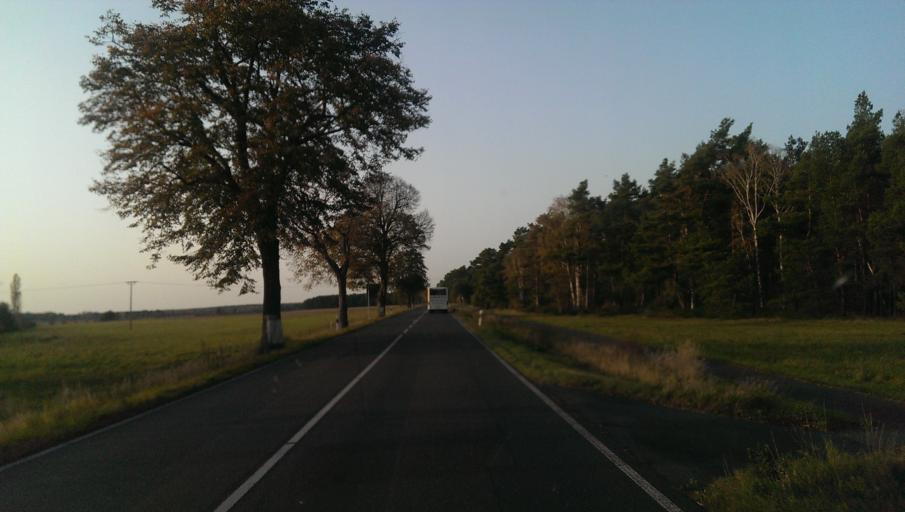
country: DE
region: Brandenburg
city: Herzberg
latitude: 51.7581
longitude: 13.2082
